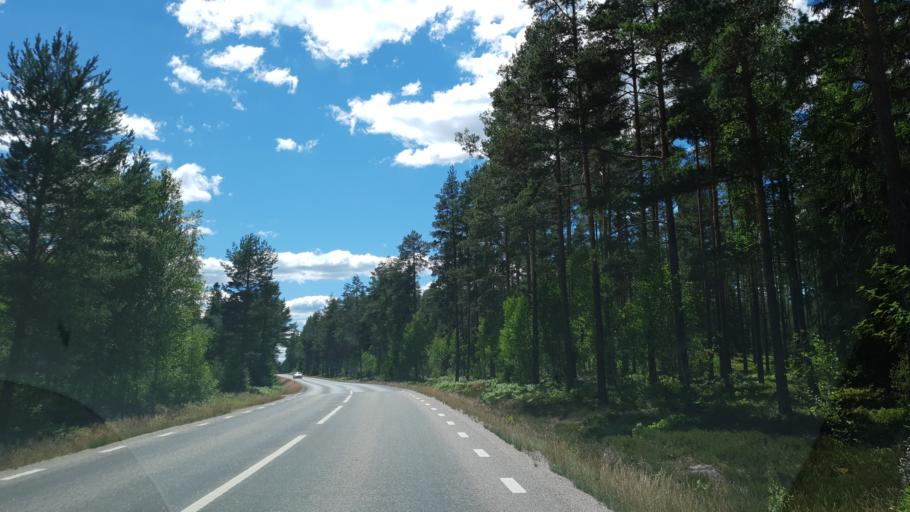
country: SE
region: Kronoberg
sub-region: Lessebo Kommun
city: Lessebo
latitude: 56.7953
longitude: 15.3170
